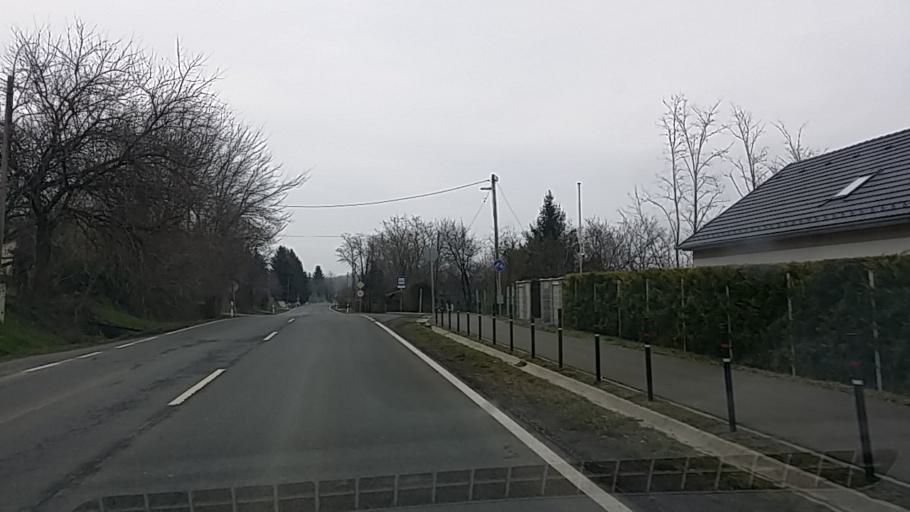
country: HU
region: Baranya
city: Mohacs
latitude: 46.0364
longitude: 18.6981
